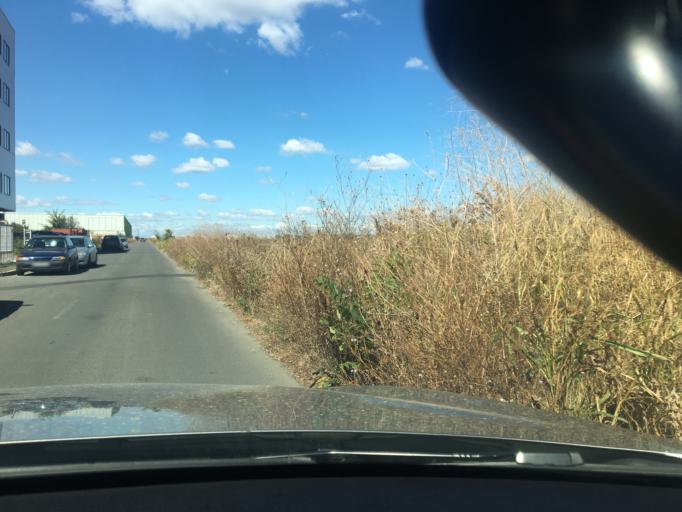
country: BG
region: Burgas
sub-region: Obshtina Burgas
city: Burgas
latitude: 42.5317
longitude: 27.4553
